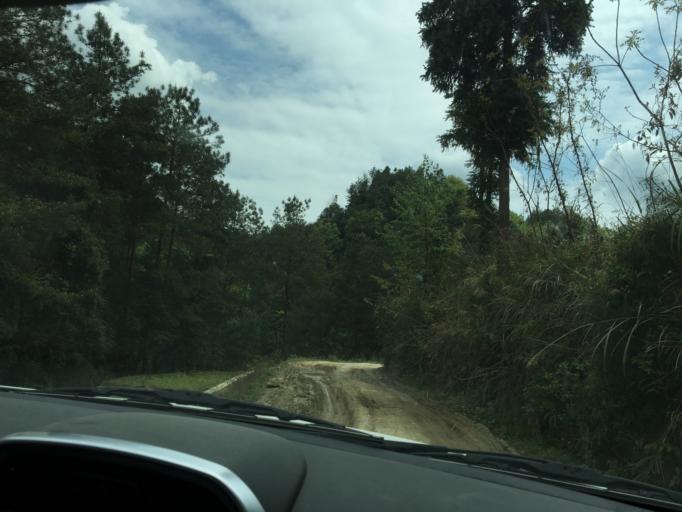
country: CN
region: Guizhou Sheng
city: Kuanping
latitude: 28.0262
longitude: 108.0514
